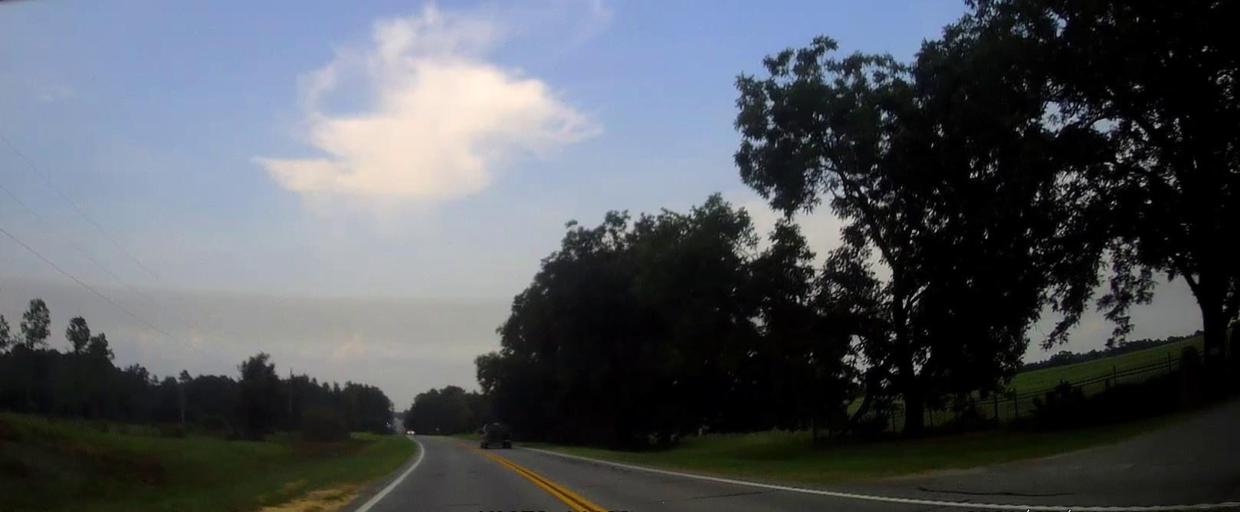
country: US
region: Georgia
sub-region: Laurens County
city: East Dublin
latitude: 32.5956
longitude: -82.8265
